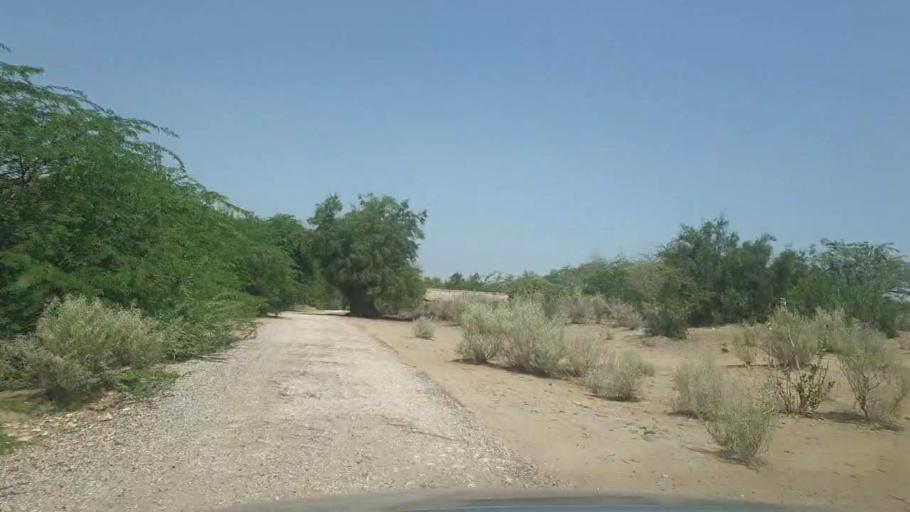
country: PK
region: Sindh
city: Kot Diji
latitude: 27.3176
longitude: 69.0613
